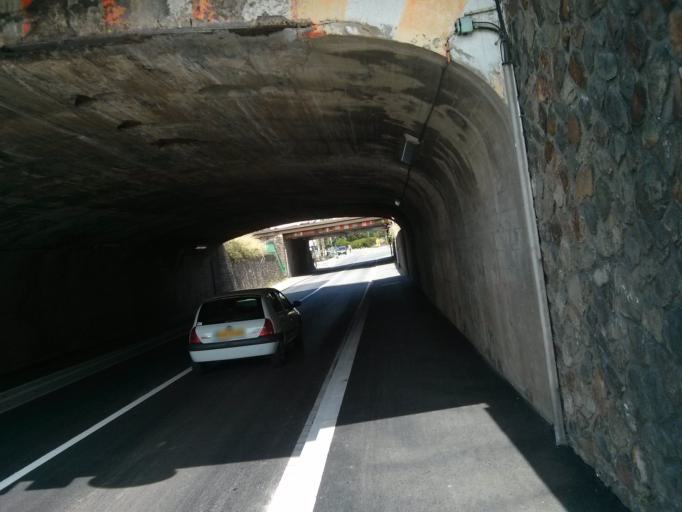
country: FR
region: Brittany
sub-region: Departement d'Ille-et-Vilaine
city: Rennes
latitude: 48.1059
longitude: -1.6505
